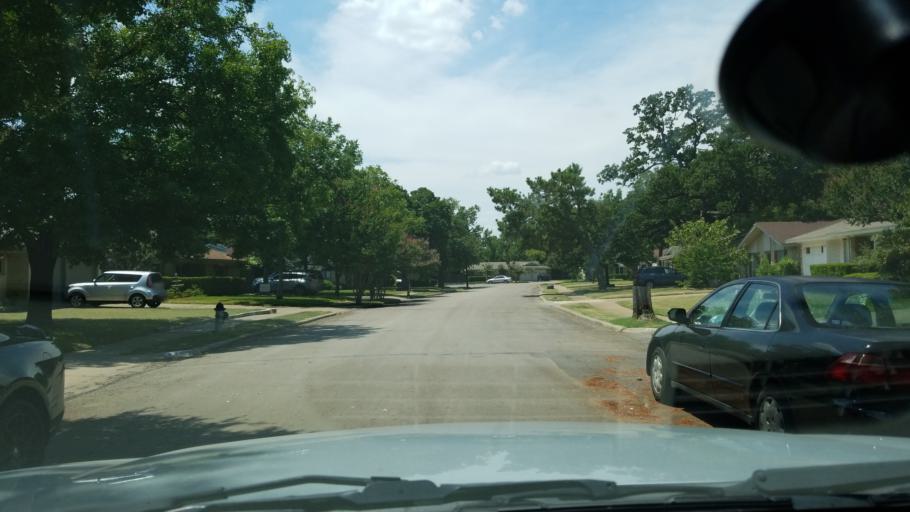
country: US
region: Texas
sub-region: Dallas County
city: Irving
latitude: 32.8271
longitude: -96.9880
